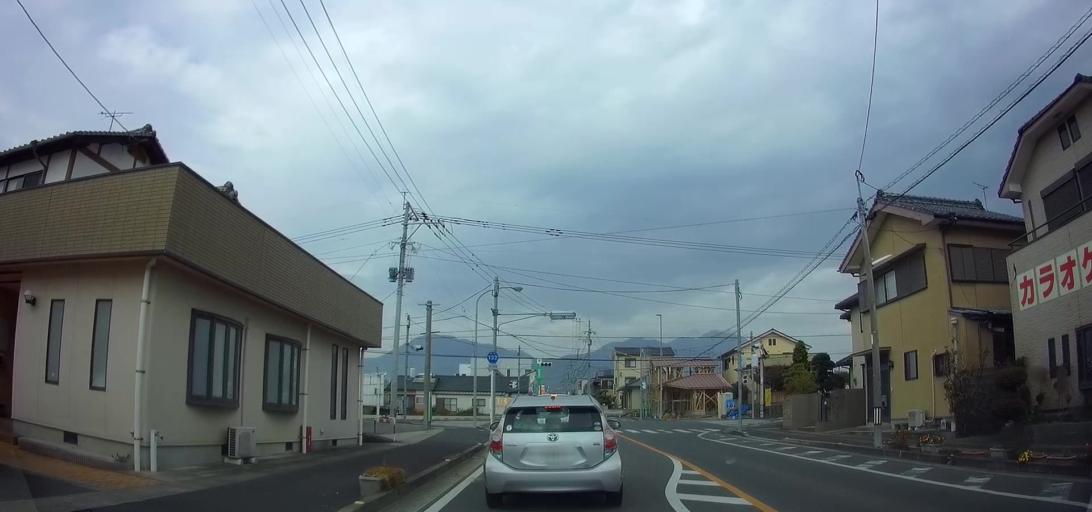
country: JP
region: Nagasaki
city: Shimabara
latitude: 32.6642
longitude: 130.3045
